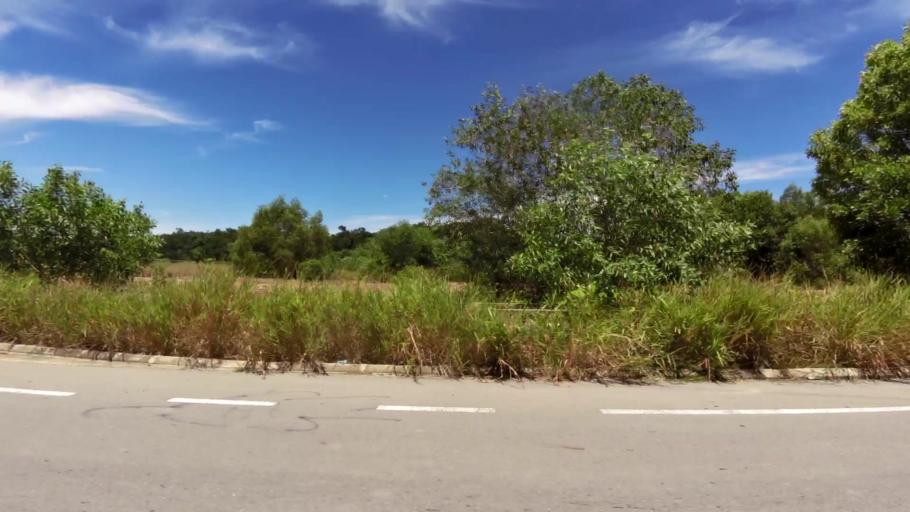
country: BN
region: Brunei and Muara
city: Bandar Seri Begawan
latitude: 5.0257
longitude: 115.0351
